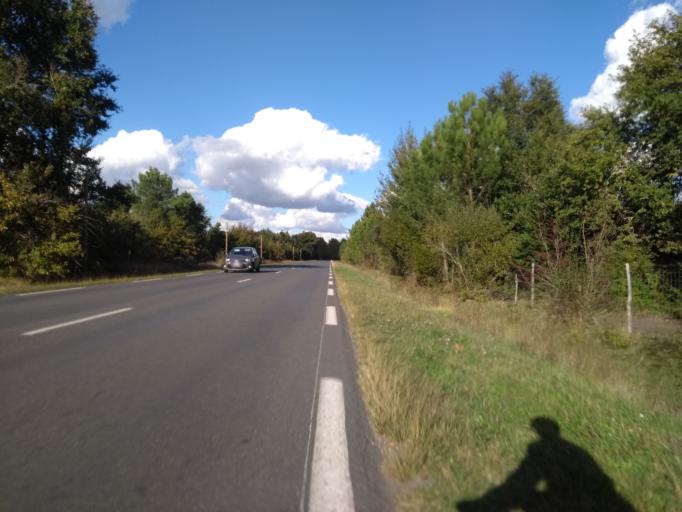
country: FR
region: Aquitaine
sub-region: Departement de la Gironde
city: Saint-Aubin-de-Medoc
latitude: 44.6753
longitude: -0.7284
